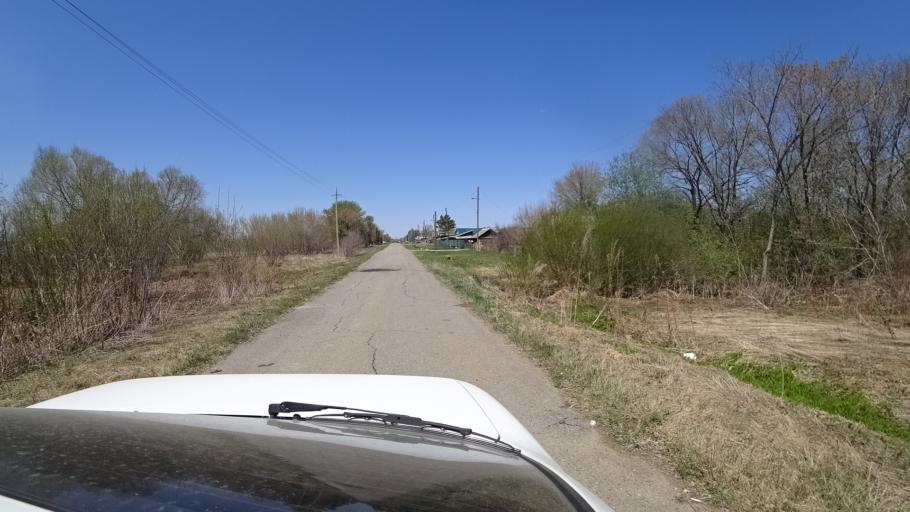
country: RU
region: Primorskiy
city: Lazo
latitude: 45.7903
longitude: 133.7680
